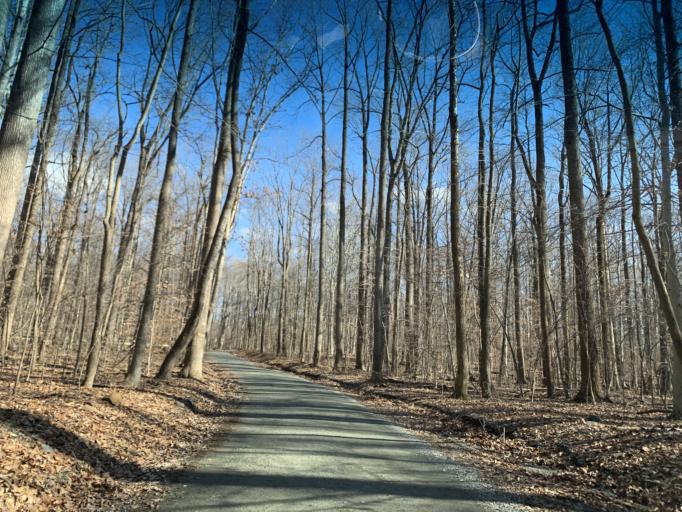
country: US
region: Maryland
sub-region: Harford County
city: Riverside
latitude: 39.5082
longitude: -76.2446
